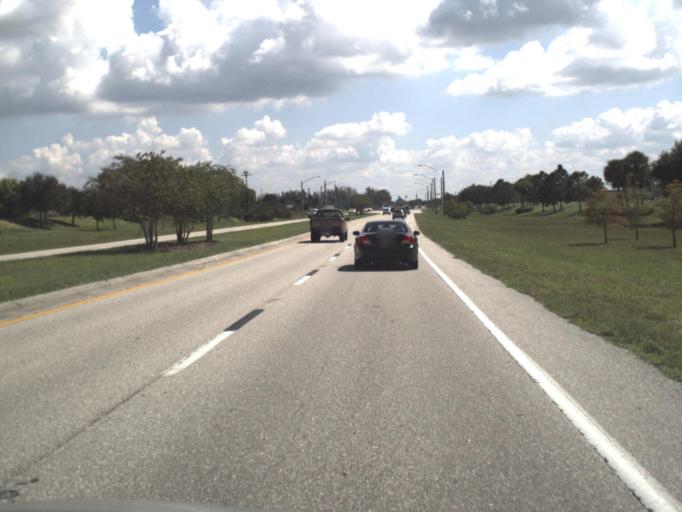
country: US
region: Florida
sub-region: Lee County
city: Cape Coral
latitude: 26.6070
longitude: -81.9955
